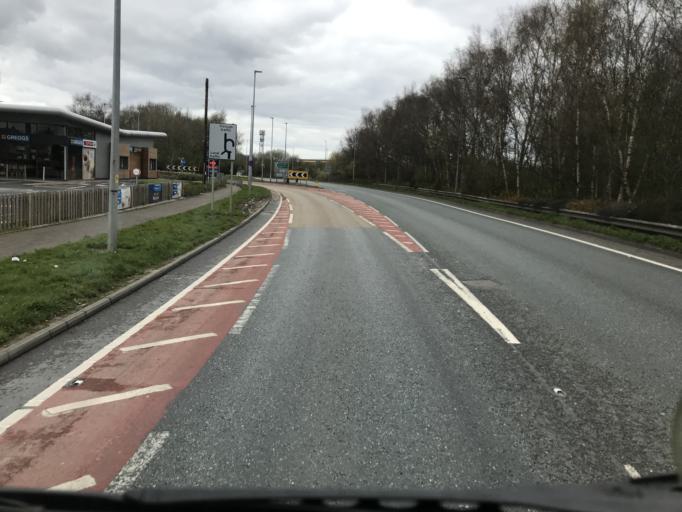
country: GB
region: England
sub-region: City and Borough of Salford
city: Irlam
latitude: 53.4561
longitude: -2.4010
